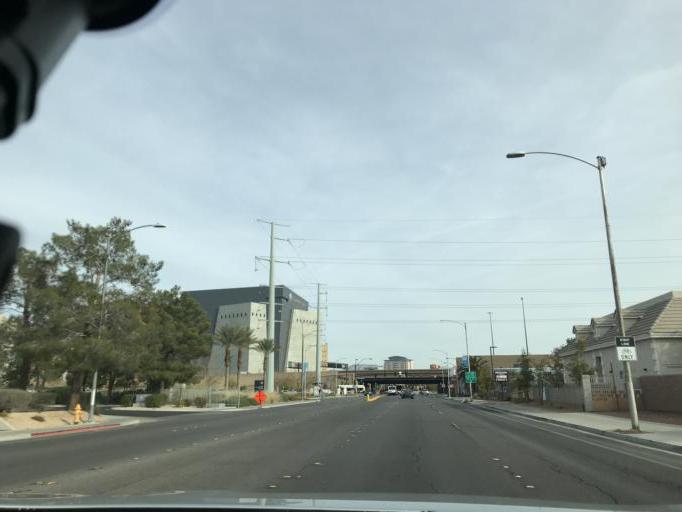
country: US
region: Nevada
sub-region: Clark County
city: Las Vegas
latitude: 36.1662
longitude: -115.1634
